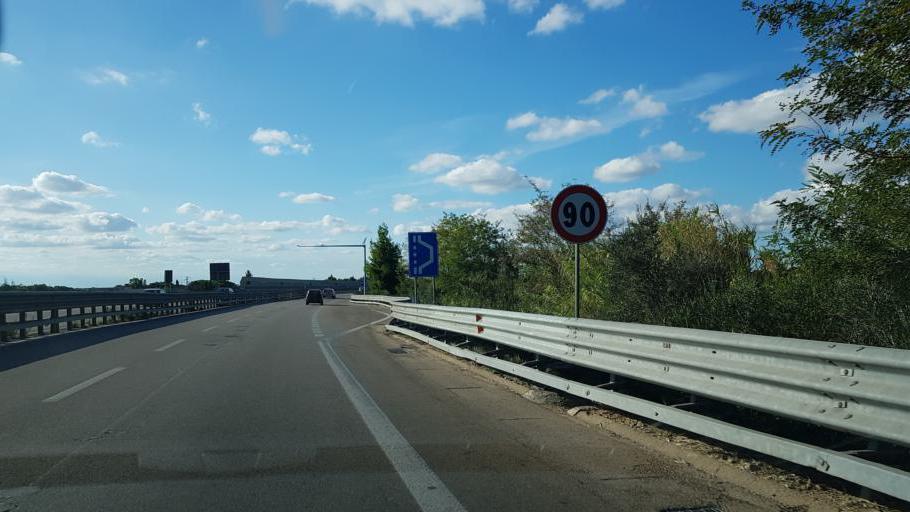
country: IT
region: Apulia
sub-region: Provincia di Lecce
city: Lequile
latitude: 40.3268
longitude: 18.1453
